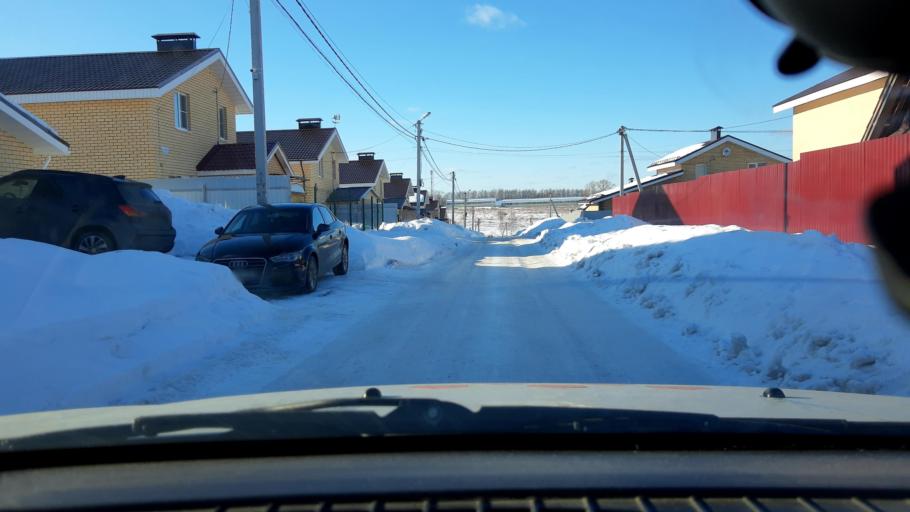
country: RU
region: Nizjnij Novgorod
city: Burevestnik
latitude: 56.1665
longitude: 43.7712
